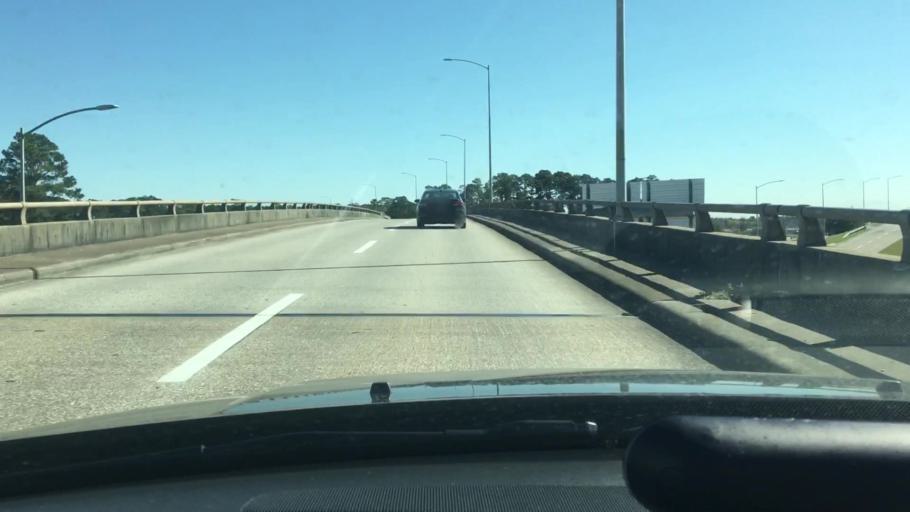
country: US
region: Texas
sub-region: Harris County
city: Humble
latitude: 29.9855
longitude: -95.3275
